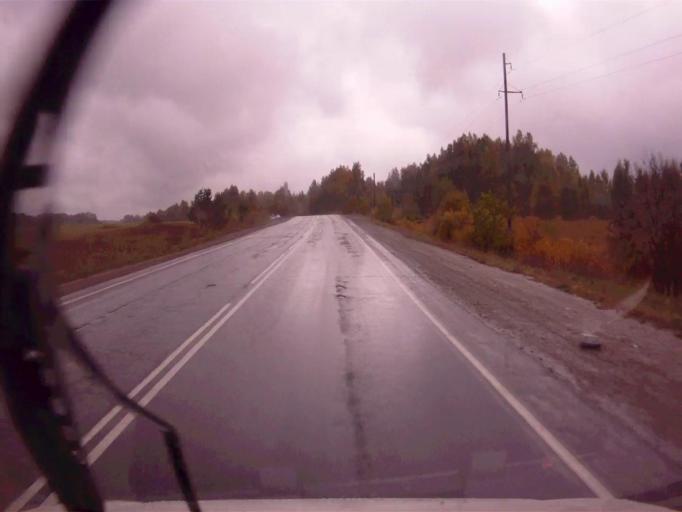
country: RU
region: Chelyabinsk
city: Argayash
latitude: 55.4853
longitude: 60.7399
